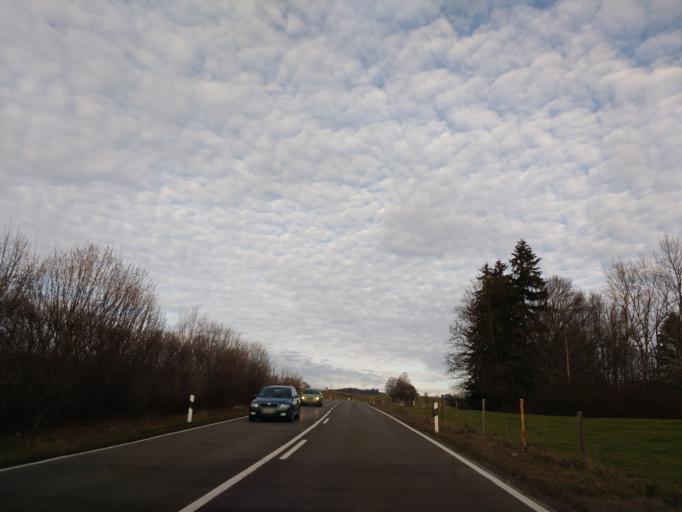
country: DE
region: Bavaria
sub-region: Swabia
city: Neuburg
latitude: 47.7717
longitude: 10.3431
